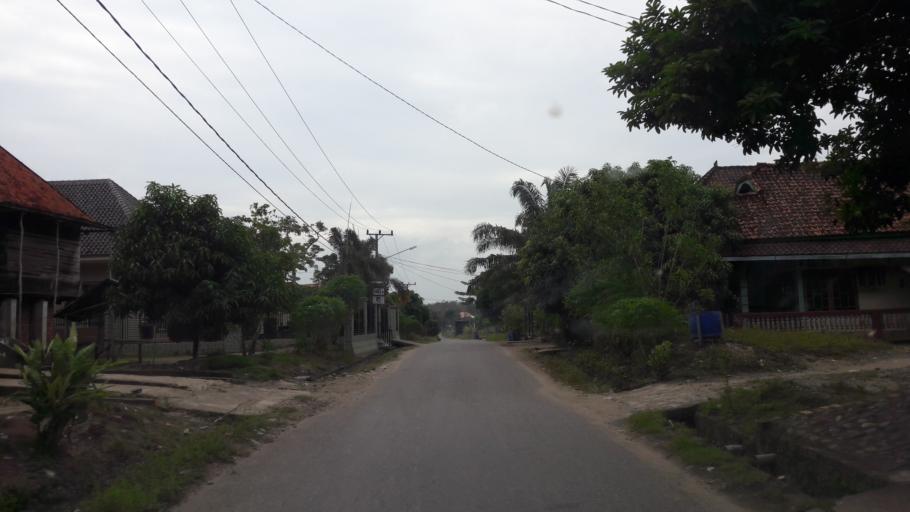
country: ID
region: South Sumatra
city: Gunungmenang
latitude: -3.1472
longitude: 104.1150
